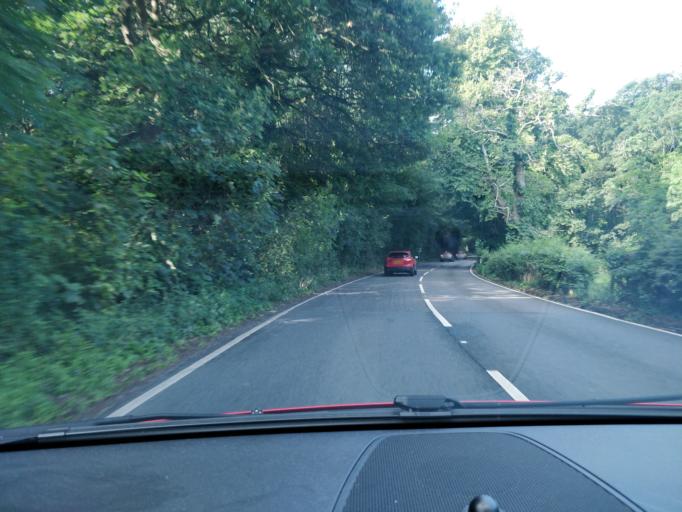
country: GB
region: Wales
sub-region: Conwy
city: Llansantffraid Glan Conwy
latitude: 53.2417
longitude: -3.7973
